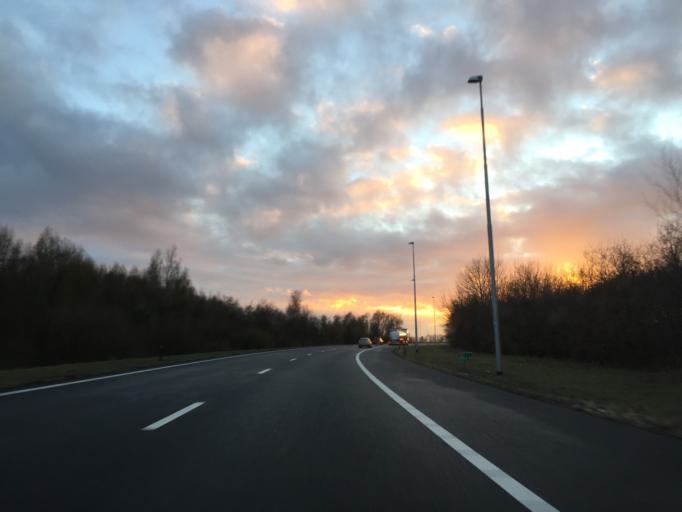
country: NL
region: Flevoland
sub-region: Gemeente Noordoostpolder
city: Emmeloord
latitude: 52.6942
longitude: 5.7725
